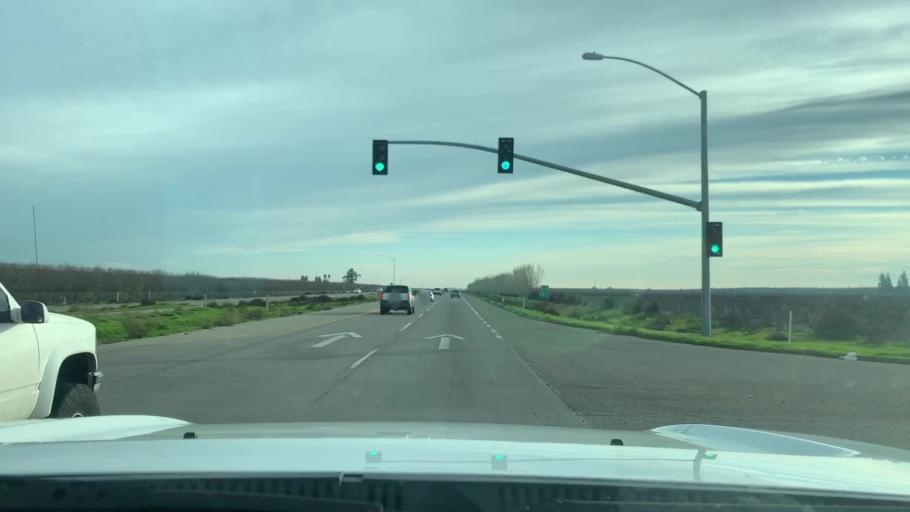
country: US
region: California
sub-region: Fresno County
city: Caruthers
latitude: 36.5182
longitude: -119.7864
